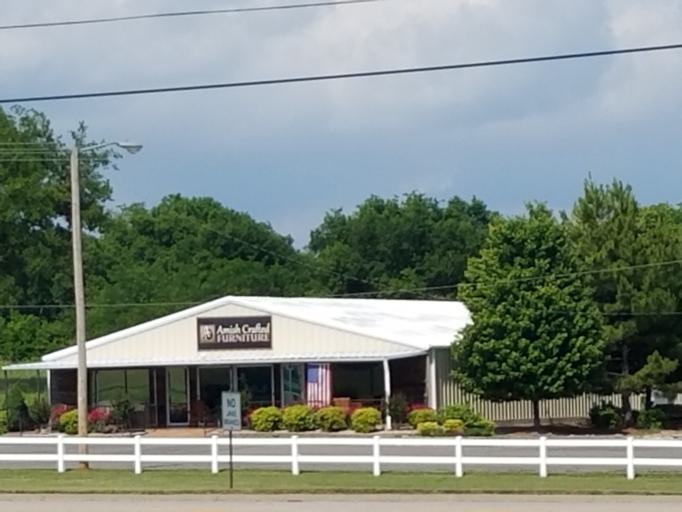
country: US
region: Oklahoma
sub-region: Mayes County
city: Chouteau
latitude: 36.1631
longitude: -95.3425
